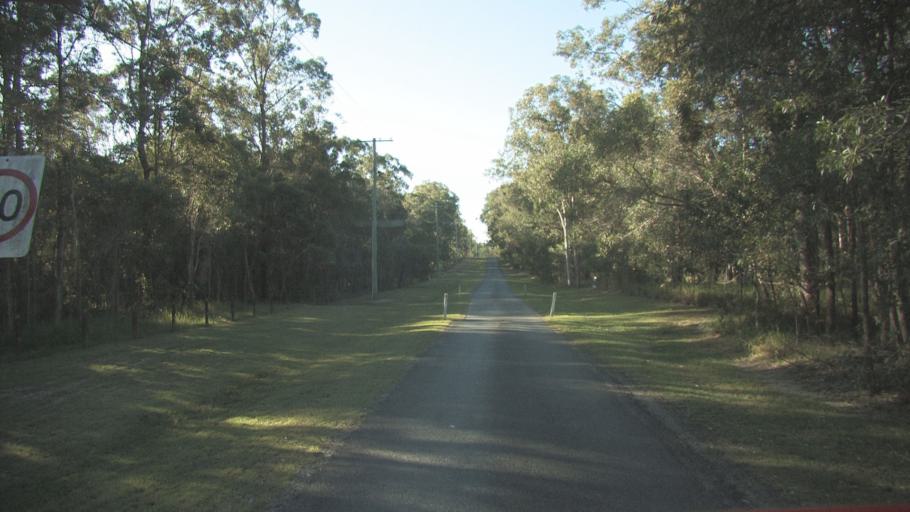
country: AU
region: Queensland
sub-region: Gold Coast
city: Yatala
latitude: -27.6677
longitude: 153.2446
